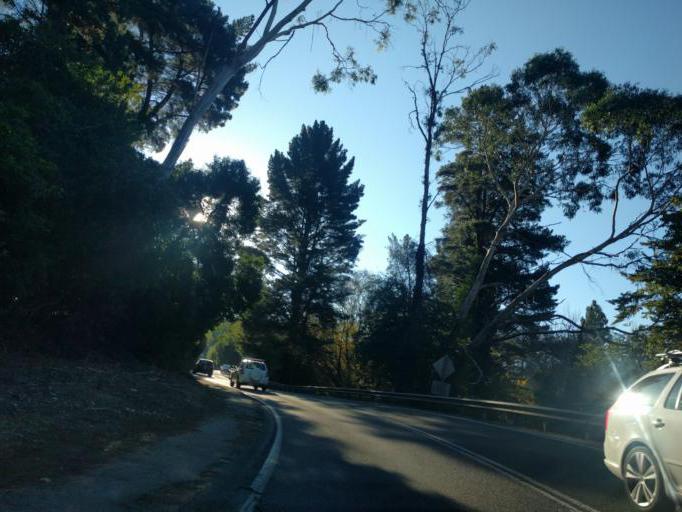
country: AU
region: South Australia
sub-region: Adelaide Hills
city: Aldgate
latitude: -35.0093
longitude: 138.7300
